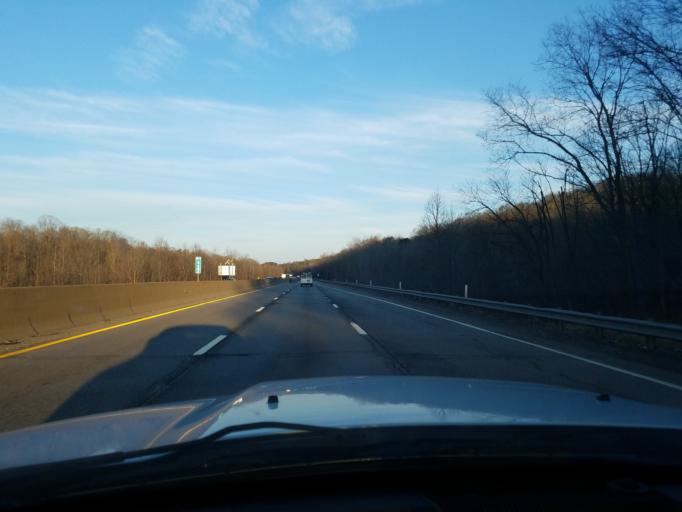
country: US
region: West Virginia
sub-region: Kanawha County
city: Nitro
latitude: 38.4497
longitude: -81.8525
